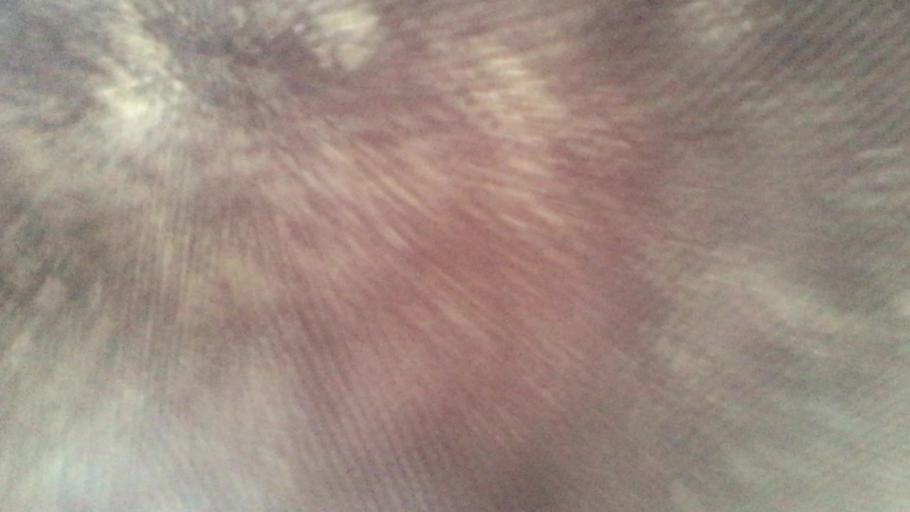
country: US
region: New Jersey
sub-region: Hudson County
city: Guttenberg
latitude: 40.7880
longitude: -73.9951
